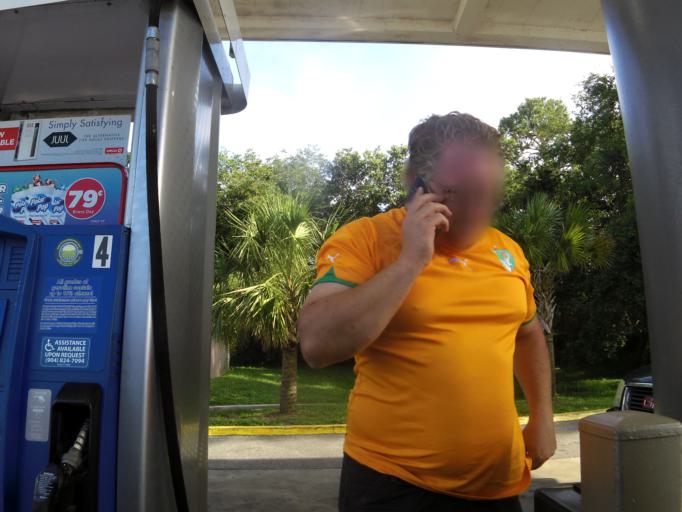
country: US
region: Florida
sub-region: Saint Johns County
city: Saint Augustine
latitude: 29.9160
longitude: -81.3461
